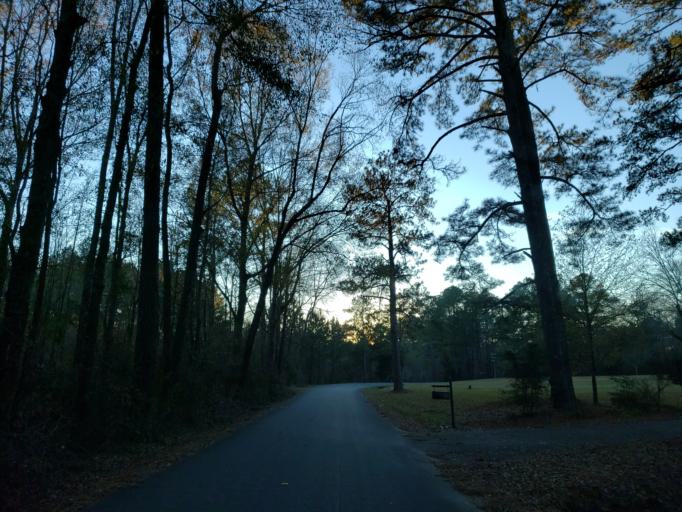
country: US
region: Mississippi
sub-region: Covington County
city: Collins
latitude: 31.5641
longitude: -89.4871
